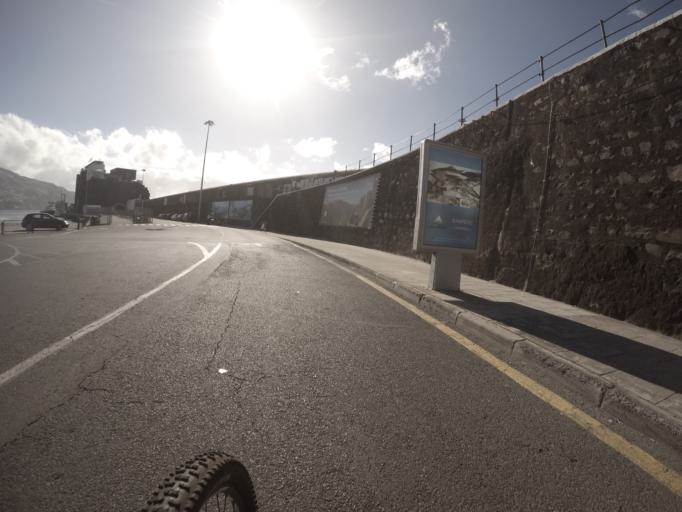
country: PT
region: Madeira
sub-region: Funchal
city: Funchal
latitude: 32.6413
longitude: -16.9175
